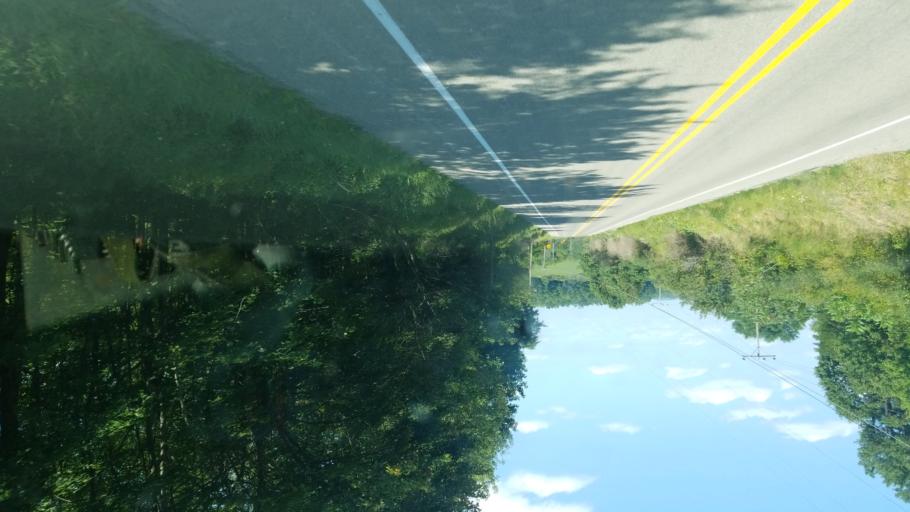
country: US
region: Pennsylvania
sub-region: Clarion County
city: Knox
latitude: 41.1094
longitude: -79.6042
